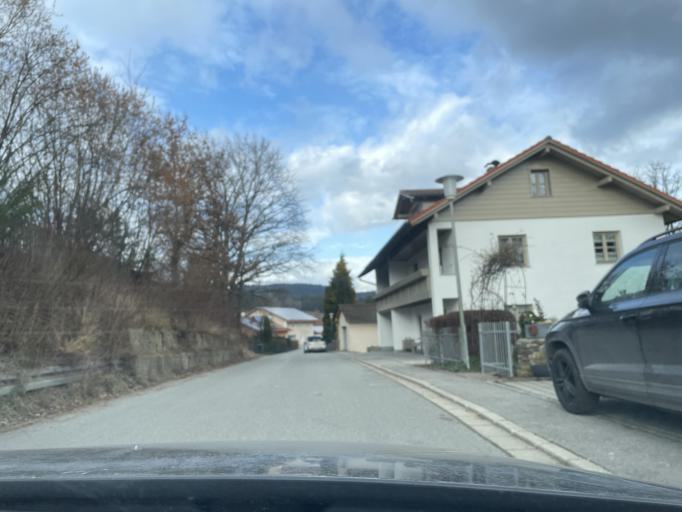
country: DE
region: Bavaria
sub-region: Lower Bavaria
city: Viechtach
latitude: 49.0867
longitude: 12.9061
